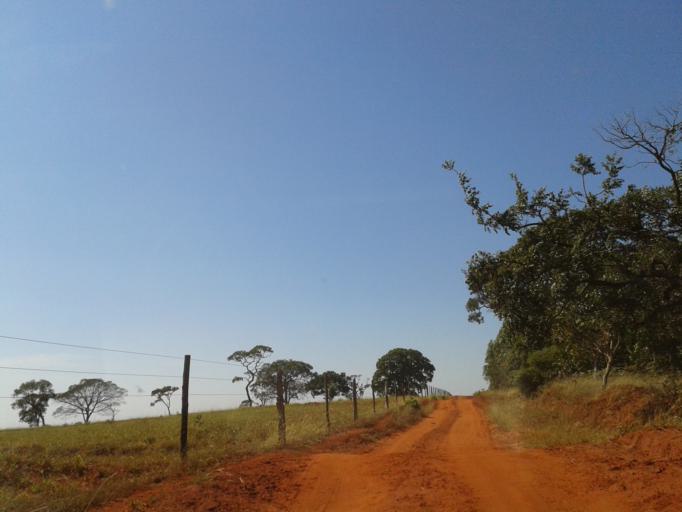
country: BR
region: Minas Gerais
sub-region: Campina Verde
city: Campina Verde
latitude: -19.4476
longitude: -49.6189
